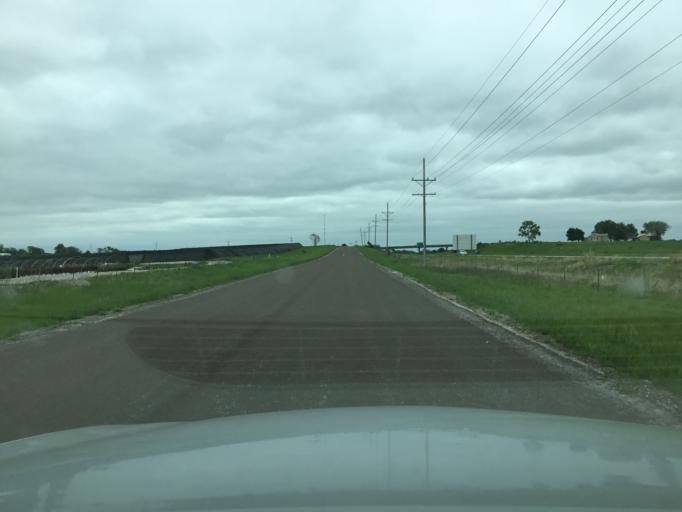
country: US
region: Kansas
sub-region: Franklin County
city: Ottawa
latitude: 38.5804
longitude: -95.2548
